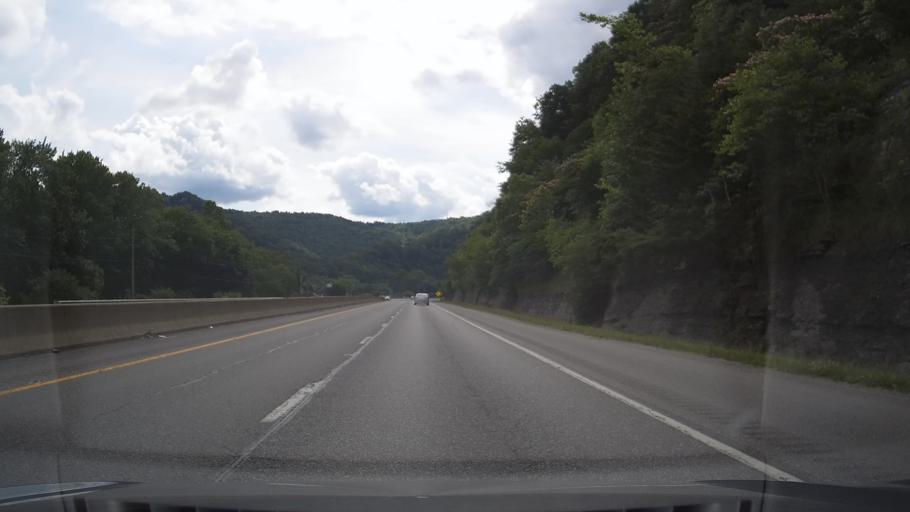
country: US
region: Kentucky
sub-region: Pike County
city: Coal Run Village
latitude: 37.5751
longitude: -82.6509
